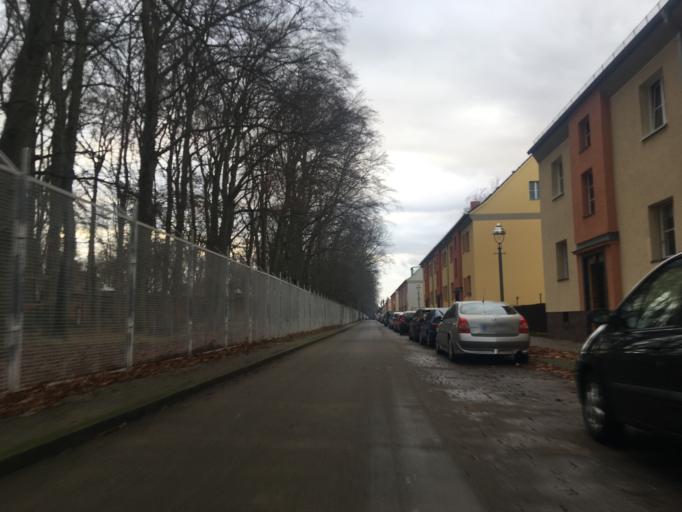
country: DE
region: Berlin
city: Wittenau
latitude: 52.5845
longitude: 13.3263
